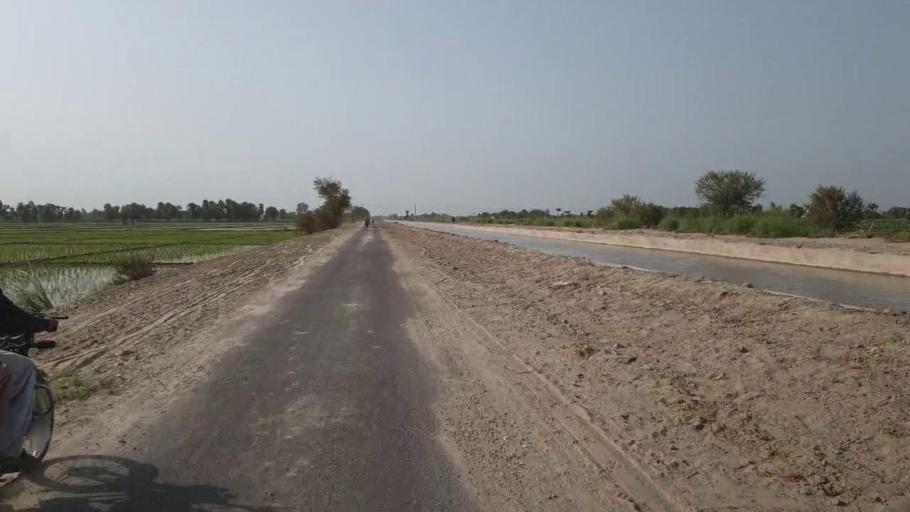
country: PK
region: Sindh
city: Daur
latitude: 26.3443
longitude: 68.1624
